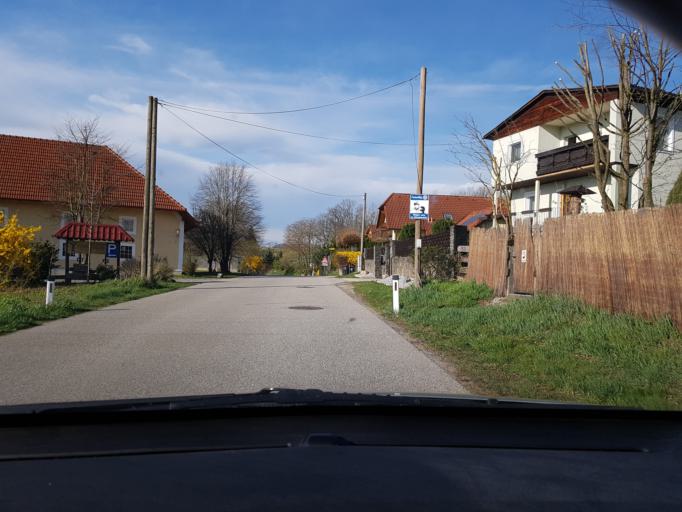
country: AT
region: Upper Austria
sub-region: Politischer Bezirk Linz-Land
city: Asten
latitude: 48.1782
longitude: 14.4146
